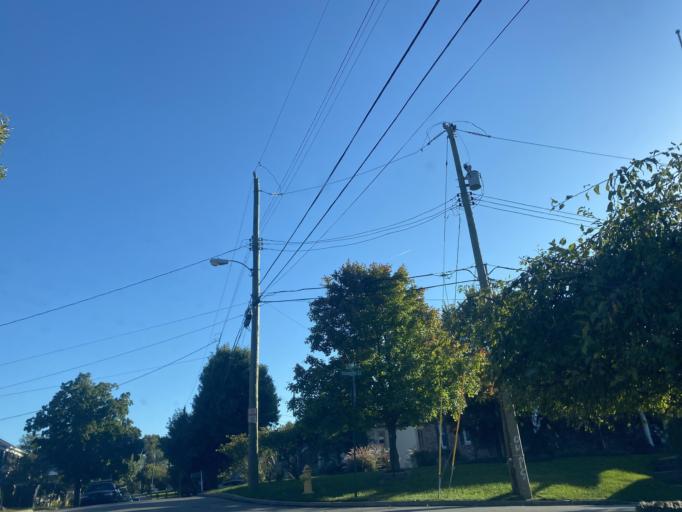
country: US
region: Kentucky
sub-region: Campbell County
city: Dayton
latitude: 39.1104
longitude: -84.4592
